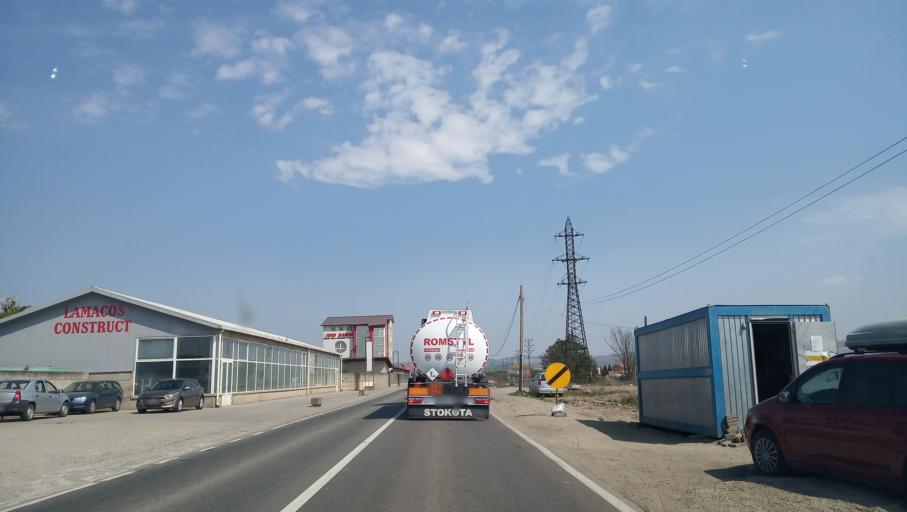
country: RO
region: Alba
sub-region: Municipiul Alba Iulia
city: Alba Iulia
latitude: 46.0524
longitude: 23.5719
